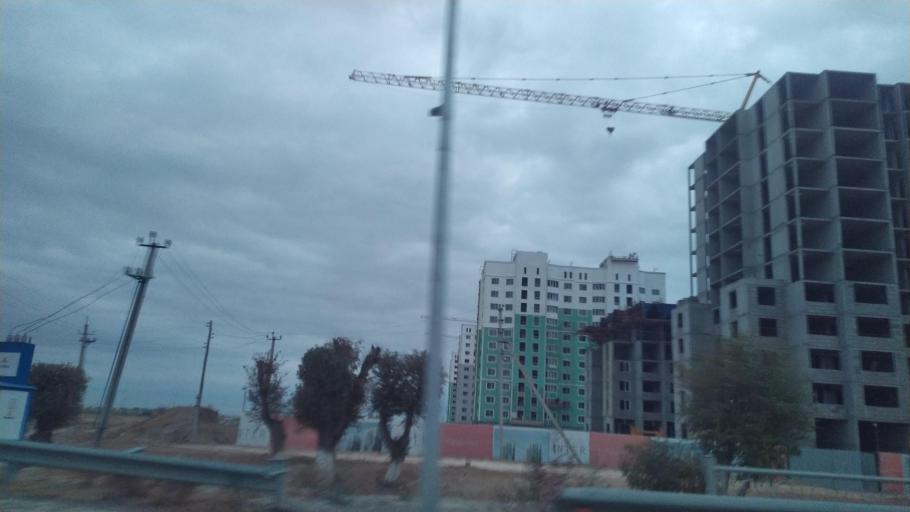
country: KZ
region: Ongtustik Qazaqstan
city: Turkestan
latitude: 43.2702
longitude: 68.3499
